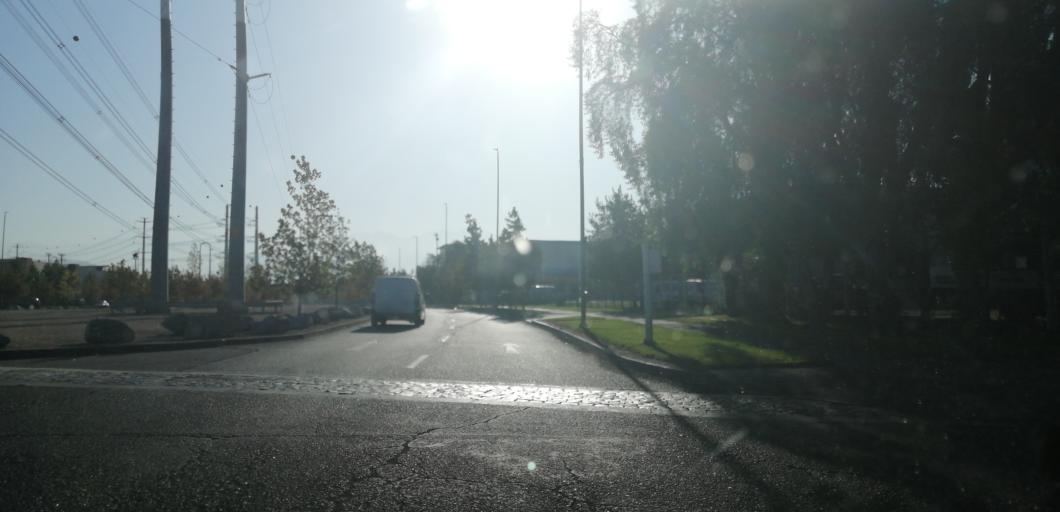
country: CL
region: Santiago Metropolitan
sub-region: Provincia de Santiago
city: Lo Prado
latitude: -33.4323
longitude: -70.7799
